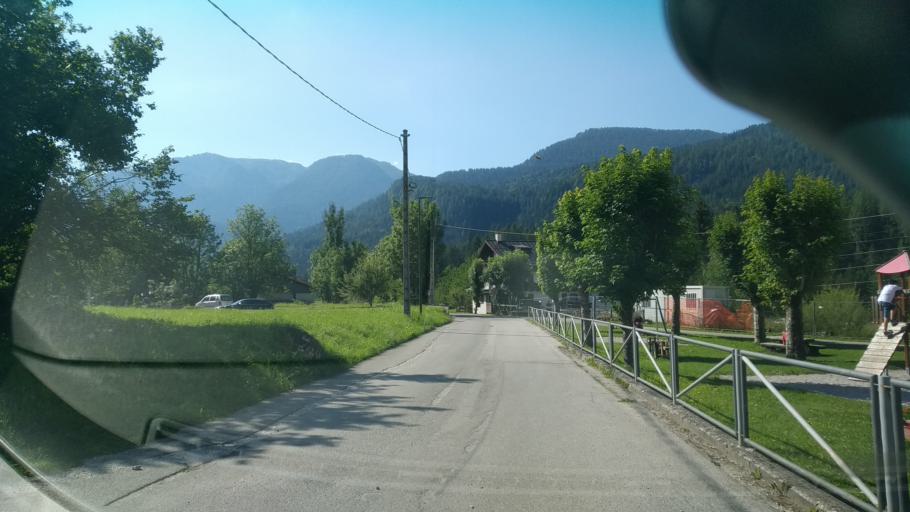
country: IT
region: Veneto
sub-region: Provincia di Belluno
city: Borca
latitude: 46.4351
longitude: 12.2184
